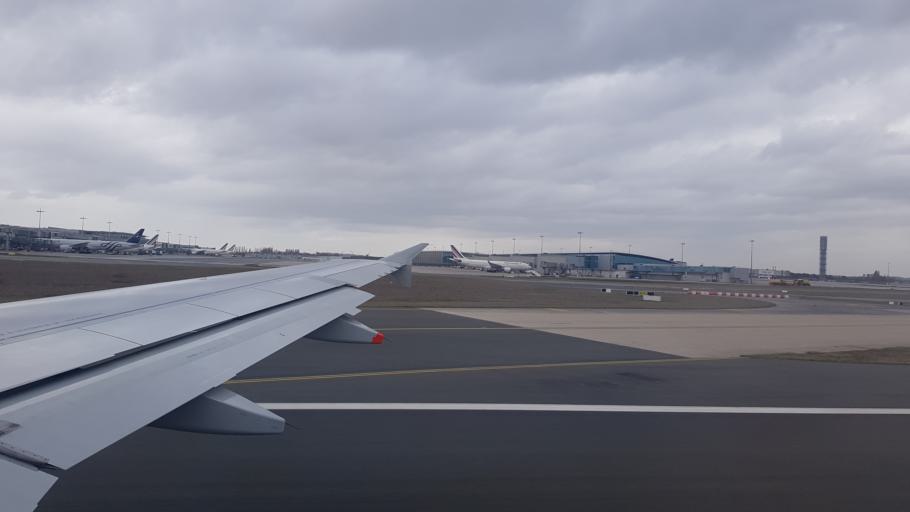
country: FR
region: Ile-de-France
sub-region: Departement de Seine-et-Marne
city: Mitry-Mory
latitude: 48.9978
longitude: 2.5901
